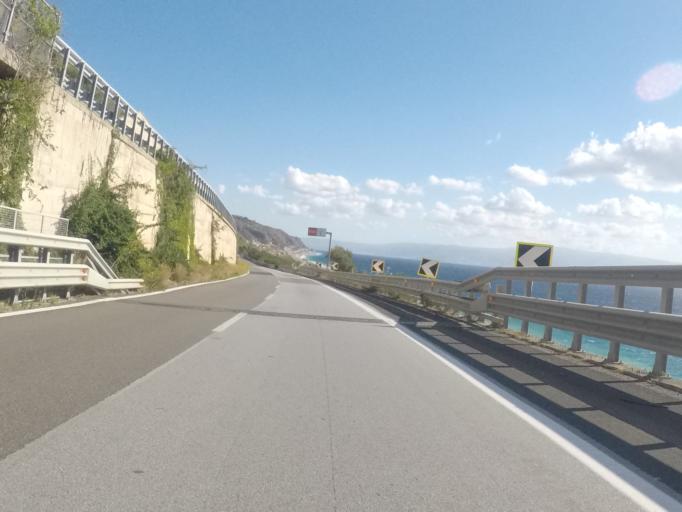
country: IT
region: Sicily
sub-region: Messina
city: Itala
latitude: 38.0306
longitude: 15.4458
